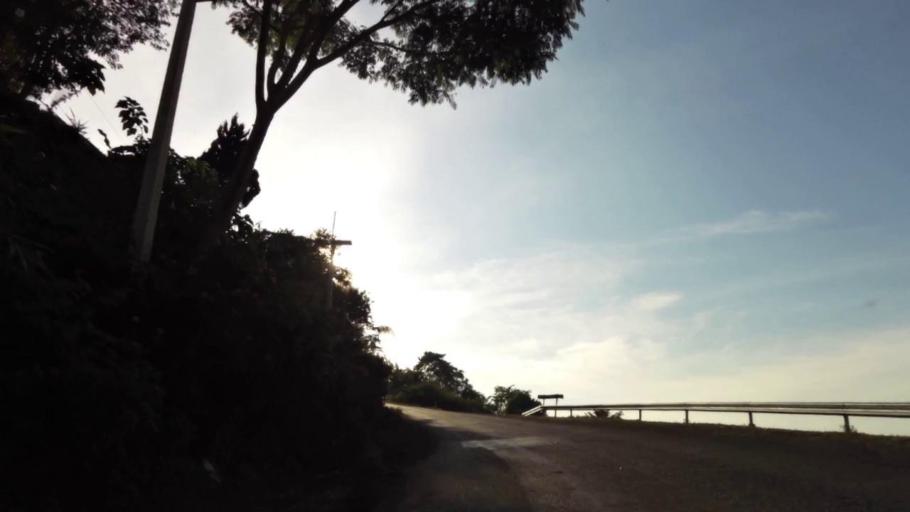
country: TH
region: Chiang Rai
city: Khun Tan
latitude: 19.8621
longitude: 100.4393
